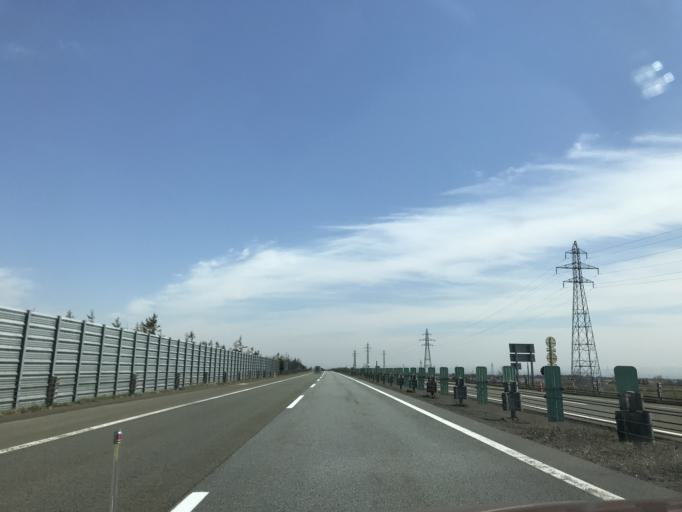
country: JP
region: Hokkaido
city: Ebetsu
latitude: 43.0869
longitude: 141.5639
